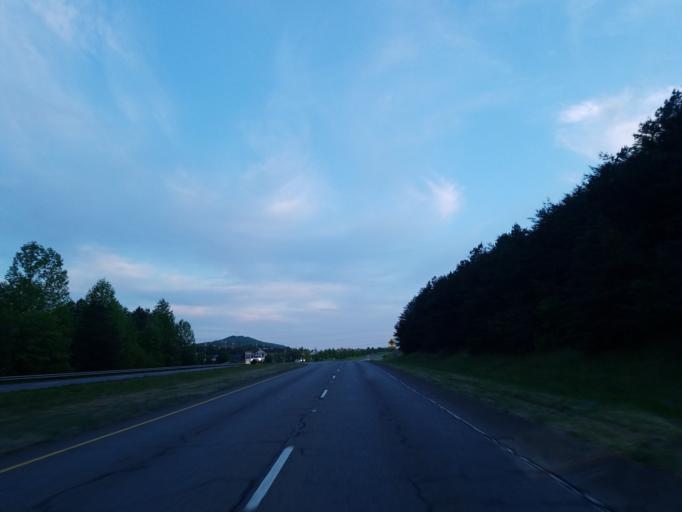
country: US
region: Georgia
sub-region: Gilmer County
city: Ellijay
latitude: 34.6670
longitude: -84.4873
